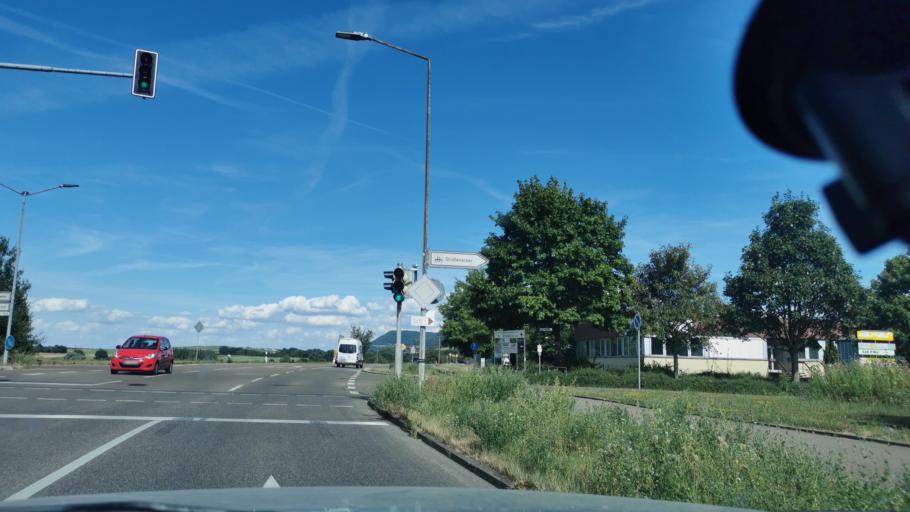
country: DE
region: Baden-Wuerttemberg
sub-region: Regierungsbezirk Stuttgart
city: Waldstetten
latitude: 48.7831
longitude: 9.8515
